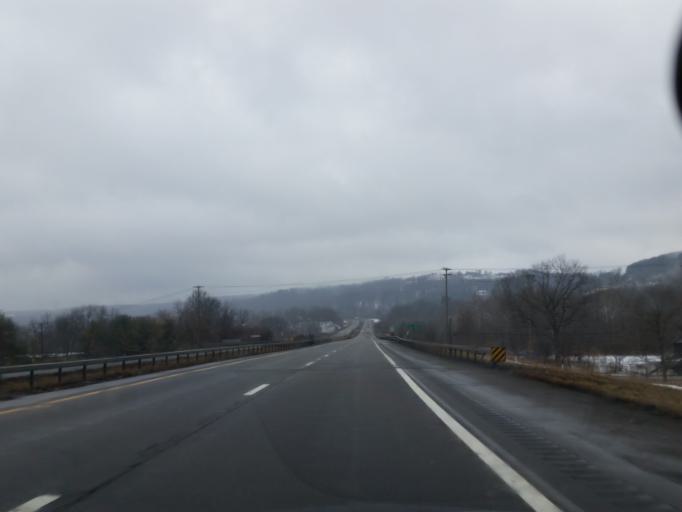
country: US
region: New York
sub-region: Chenango County
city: Lakeview
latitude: 42.3397
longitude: -75.9785
